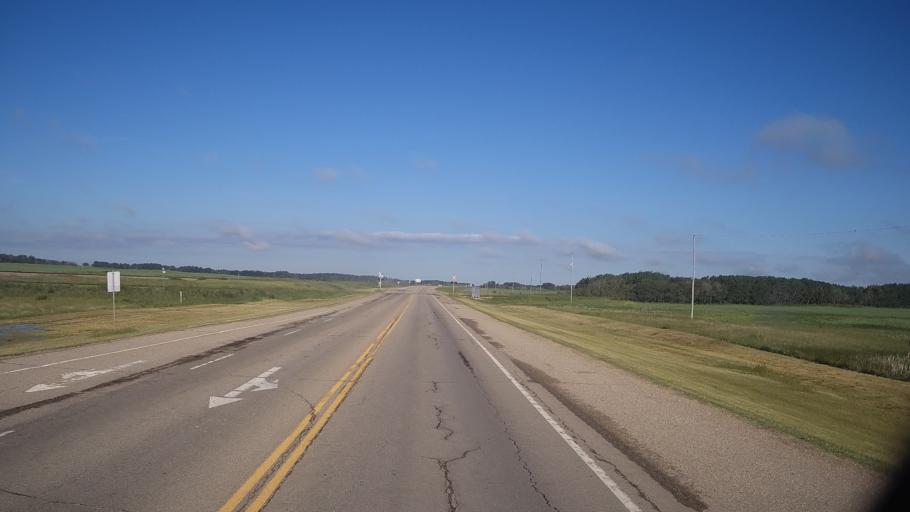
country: CA
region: Saskatchewan
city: Lanigan
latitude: 51.8494
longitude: -105.0539
